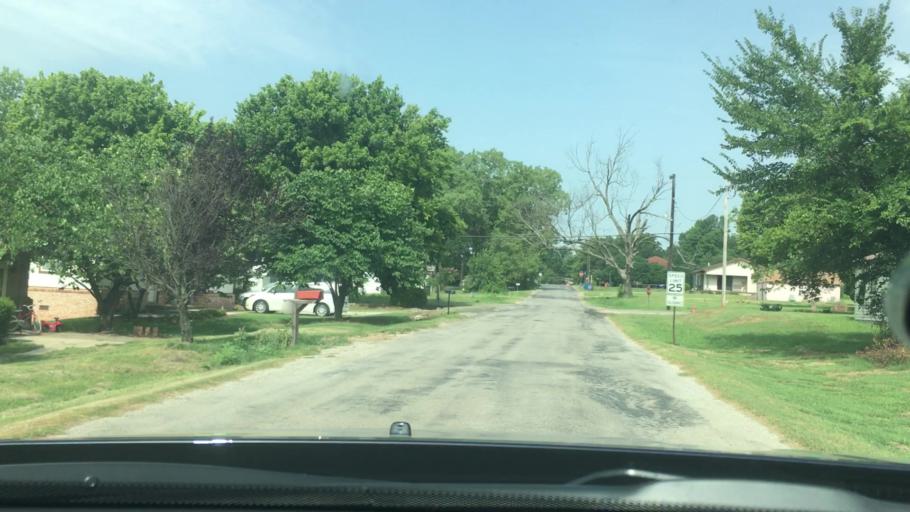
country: US
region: Oklahoma
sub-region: Garvin County
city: Pauls Valley
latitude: 34.8269
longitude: -97.2571
